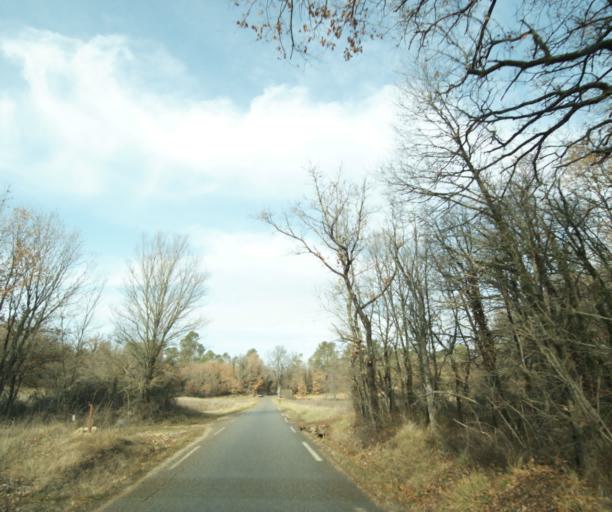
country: FR
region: Provence-Alpes-Cote d'Azur
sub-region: Departement du Var
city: Saint-Maximin-la-Sainte-Baume
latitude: 43.4221
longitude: 5.8692
